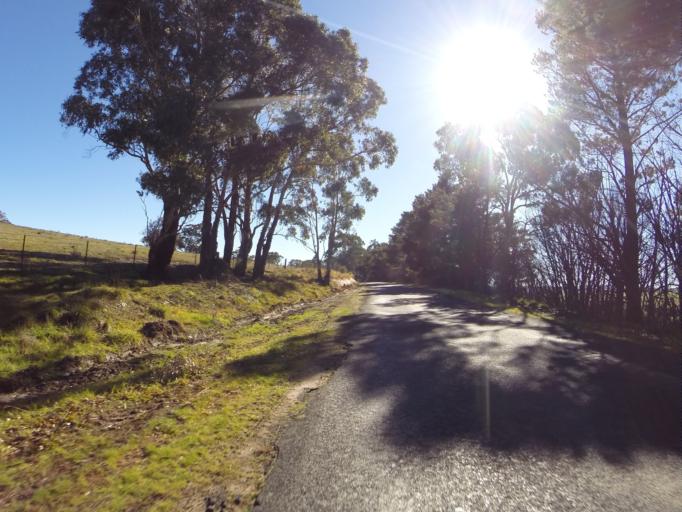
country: AU
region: New South Wales
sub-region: Oberon
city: Oberon
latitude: -33.5665
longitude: 149.8732
